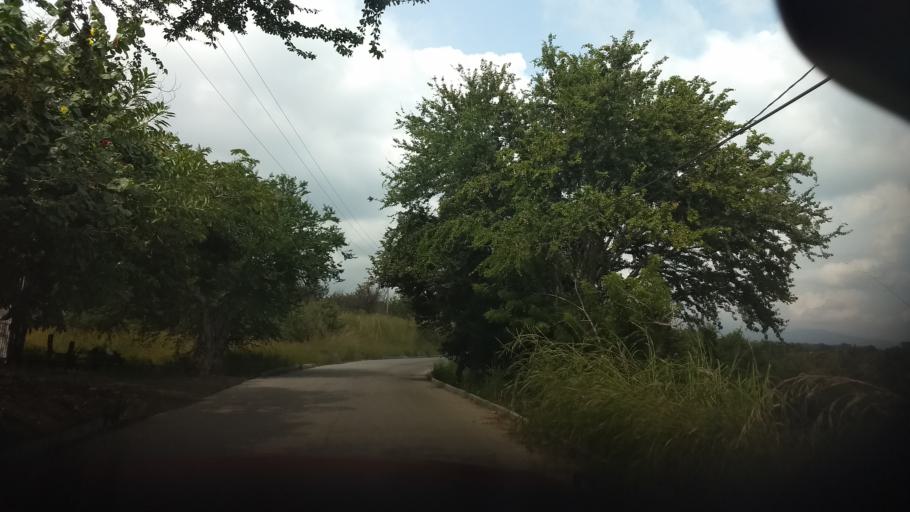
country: MX
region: Jalisco
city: Tonila
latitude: 19.3942
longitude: -103.5291
